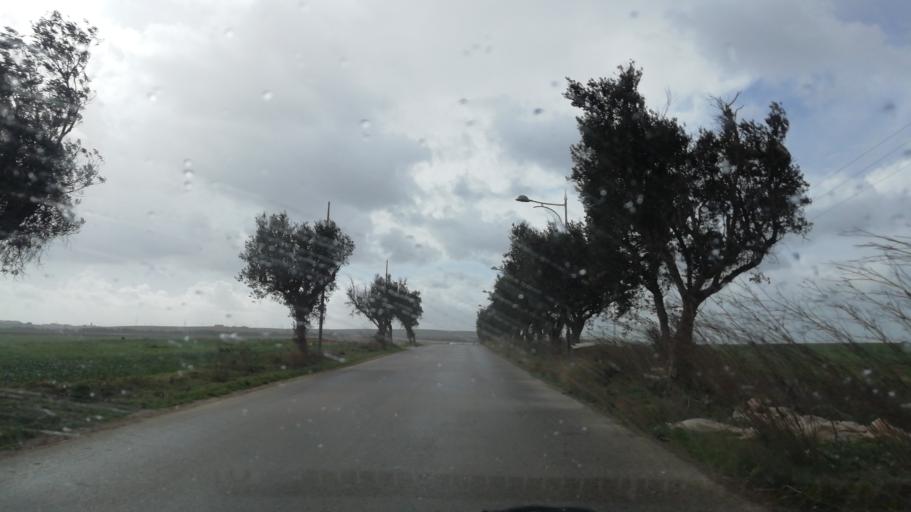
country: DZ
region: Oran
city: Sidi ech Chahmi
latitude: 35.6492
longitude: -0.5236
